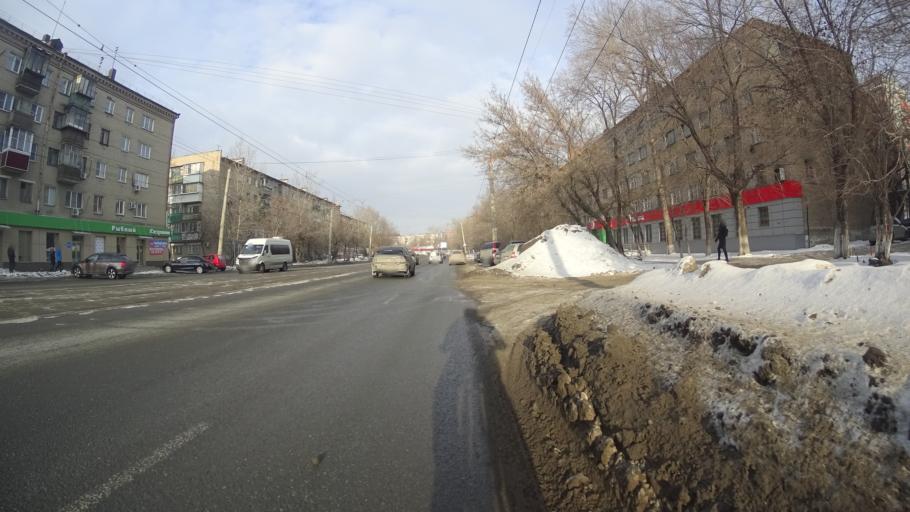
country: RU
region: Chelyabinsk
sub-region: Gorod Chelyabinsk
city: Chelyabinsk
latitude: 55.1457
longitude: 61.3881
